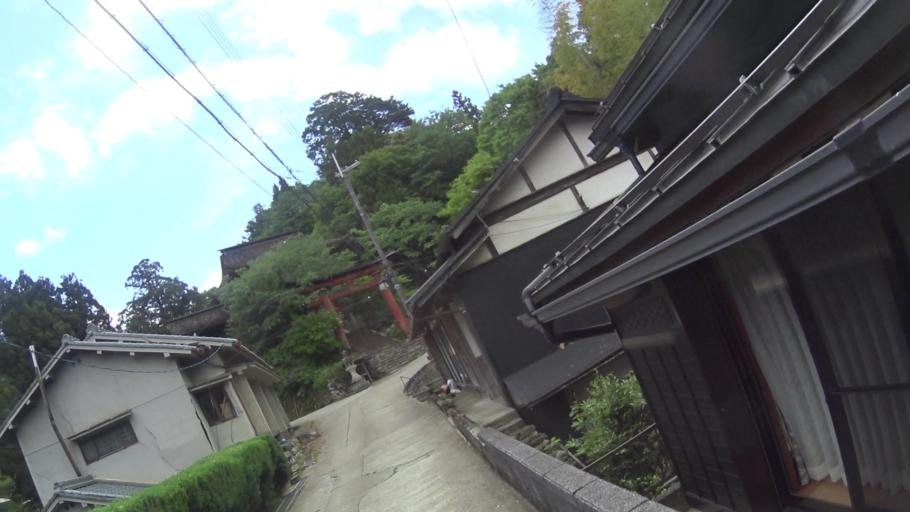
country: JP
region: Nara
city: Yoshino-cho
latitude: 34.3545
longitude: 135.8715
